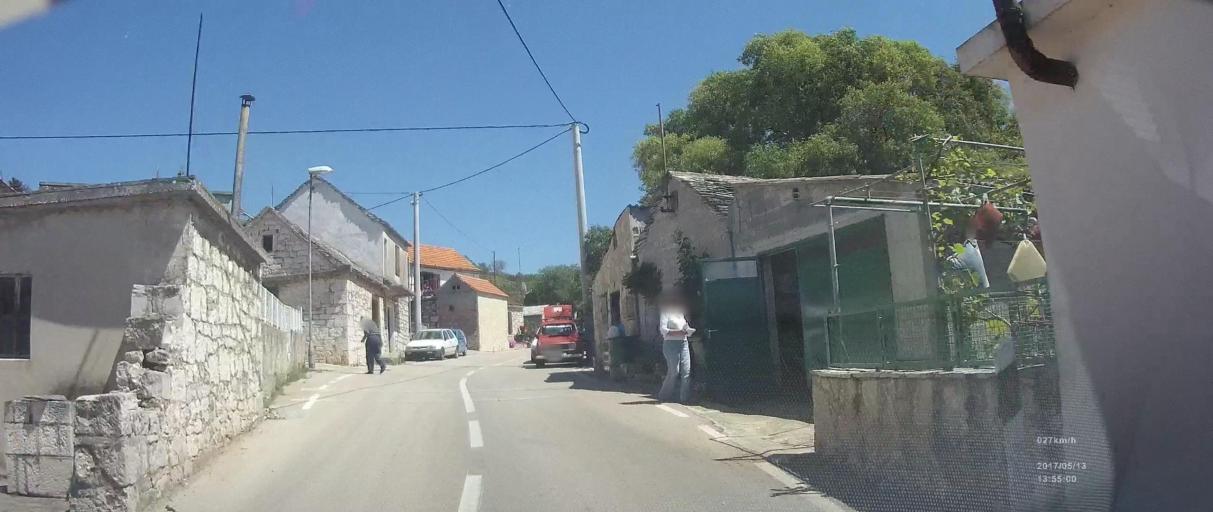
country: HR
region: Sibensko-Kniniska
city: Rogoznica
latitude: 43.5960
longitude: 16.0121
